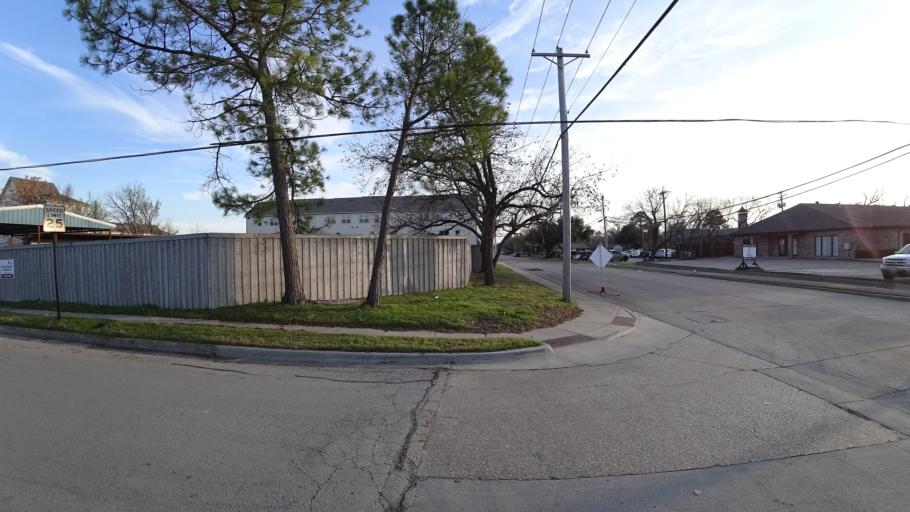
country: US
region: Texas
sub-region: Denton County
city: Lewisville
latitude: 33.0455
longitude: -96.9964
